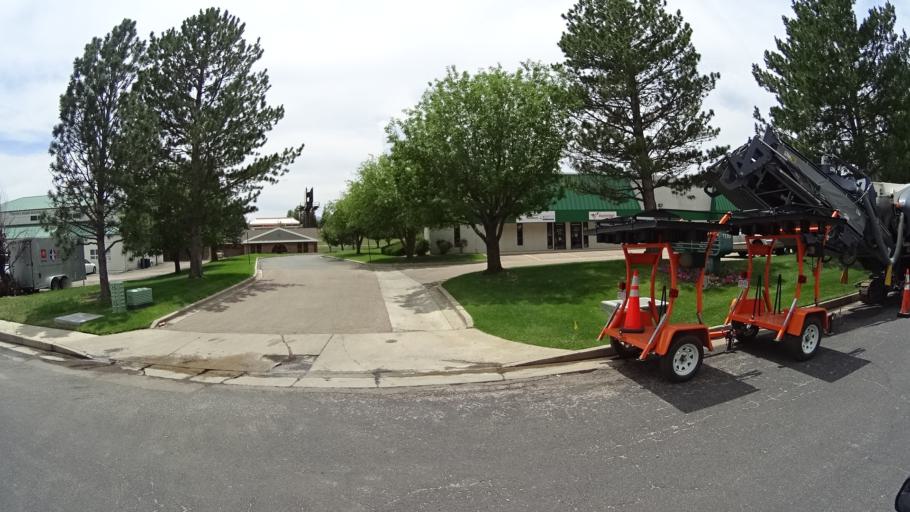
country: US
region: Colorado
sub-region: El Paso County
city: Colorado Springs
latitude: 38.8980
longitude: -104.8454
